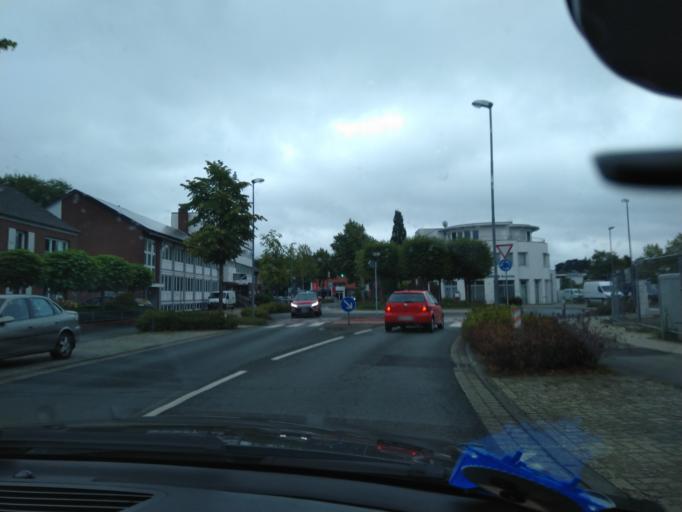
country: DE
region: Lower Saxony
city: Nordhorn
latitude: 52.4247
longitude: 7.0779
